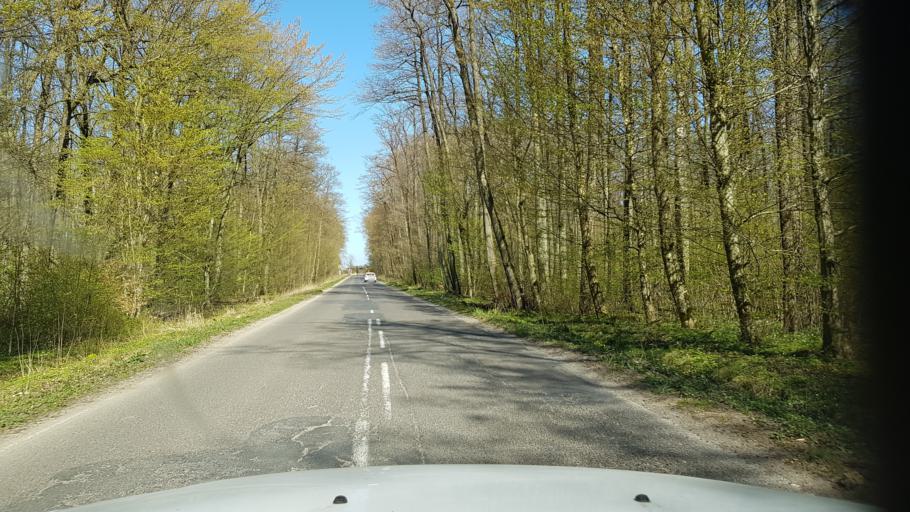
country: PL
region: West Pomeranian Voivodeship
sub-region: Koszalin
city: Koszalin
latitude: 54.2259
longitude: 16.1512
